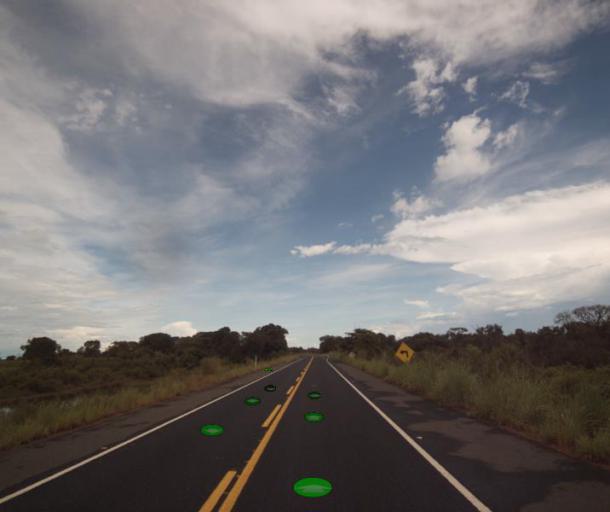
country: BR
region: Goias
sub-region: Sao Miguel Do Araguaia
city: Sao Miguel do Araguaia
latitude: -13.2297
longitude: -50.5668
